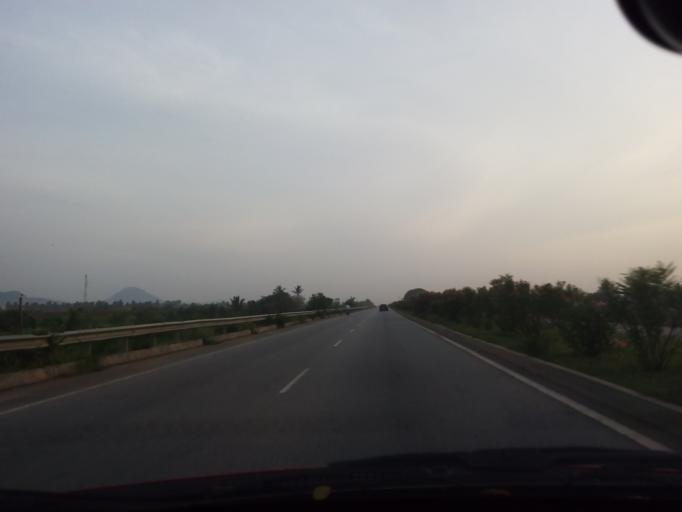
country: IN
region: Karnataka
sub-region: Bangalore Rural
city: Devanhalli
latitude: 13.3224
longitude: 77.7255
